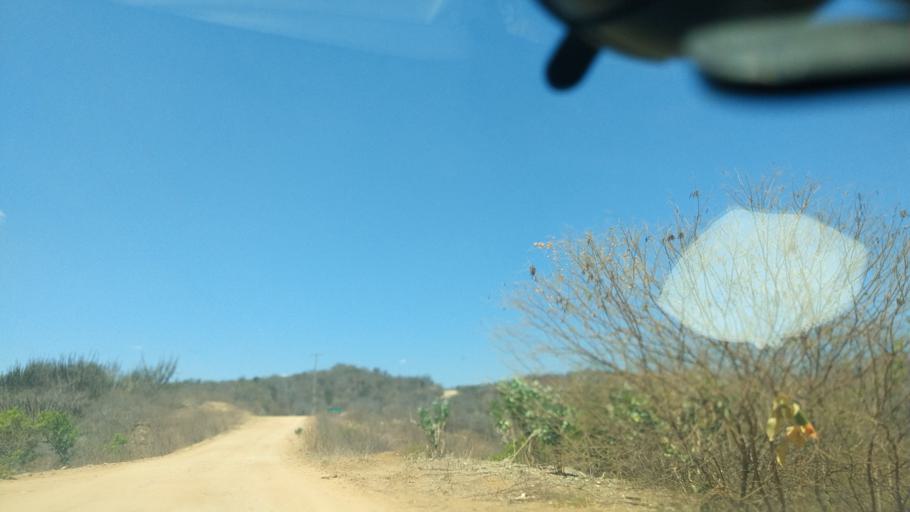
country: BR
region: Rio Grande do Norte
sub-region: Cerro Cora
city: Cerro Cora
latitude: -6.0136
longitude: -36.2754
